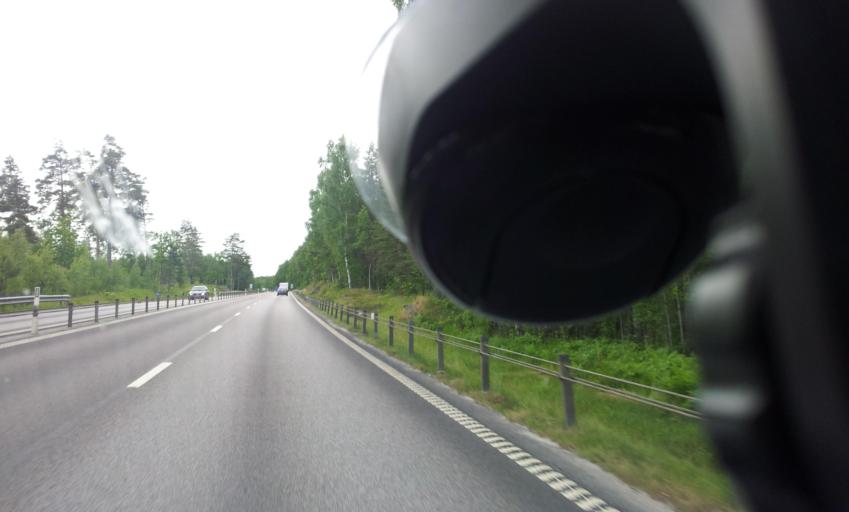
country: SE
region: Kalmar
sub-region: Oskarshamns Kommun
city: Oskarshamn
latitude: 57.3221
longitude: 16.4723
